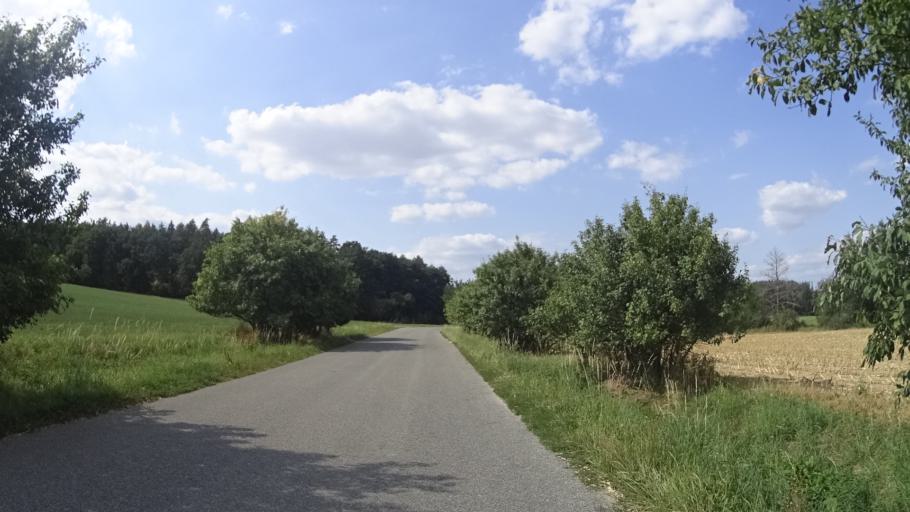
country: CZ
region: Kralovehradecky
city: Liban
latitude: 50.4165
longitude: 15.2591
